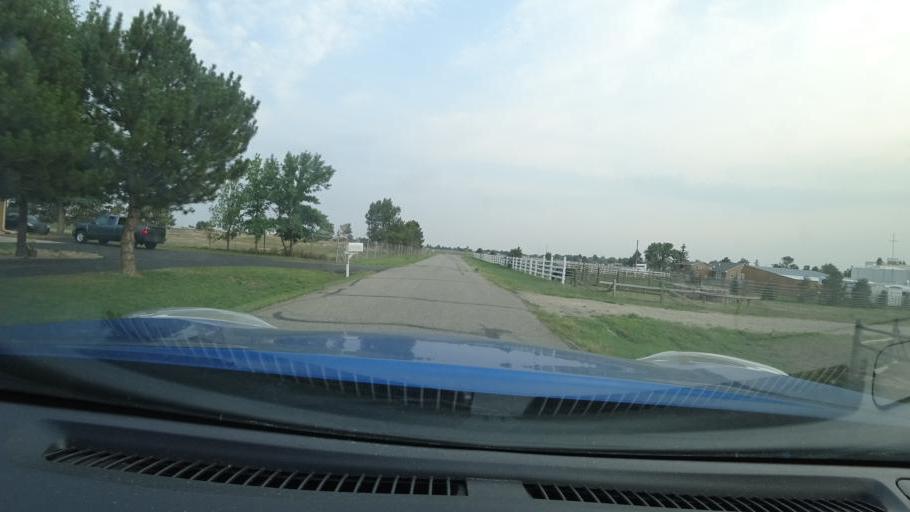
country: US
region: Colorado
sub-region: Adams County
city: Aurora
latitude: 39.7341
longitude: -104.7889
